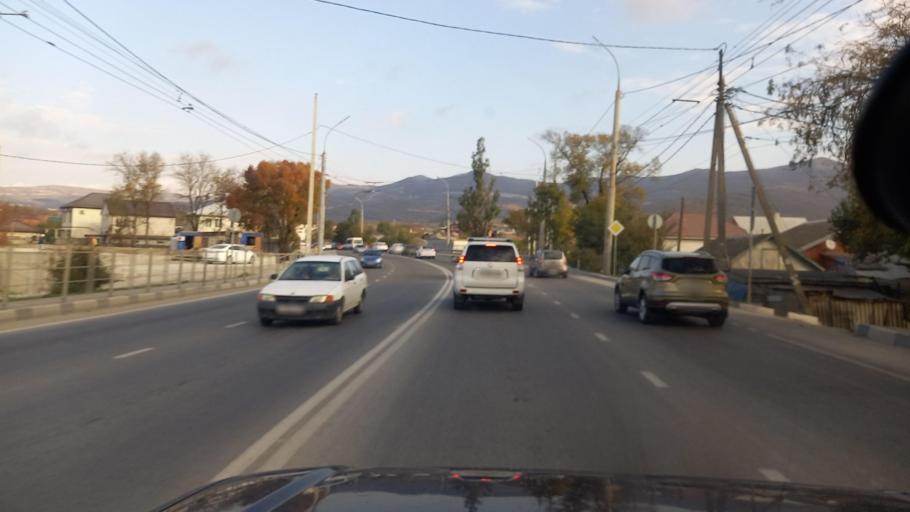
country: RU
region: Krasnodarskiy
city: Gayduk
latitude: 44.7504
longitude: 37.7273
